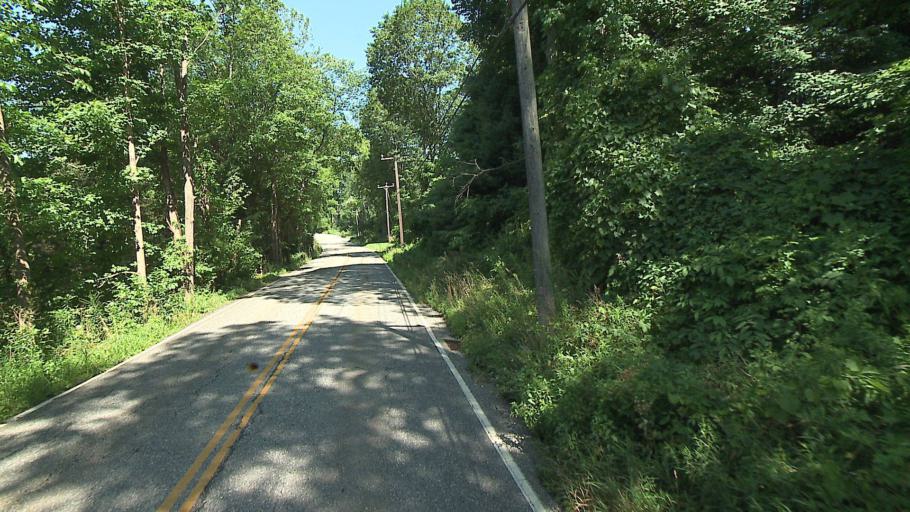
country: US
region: Connecticut
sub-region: Litchfield County
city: Kent
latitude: 41.8895
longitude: -73.4796
